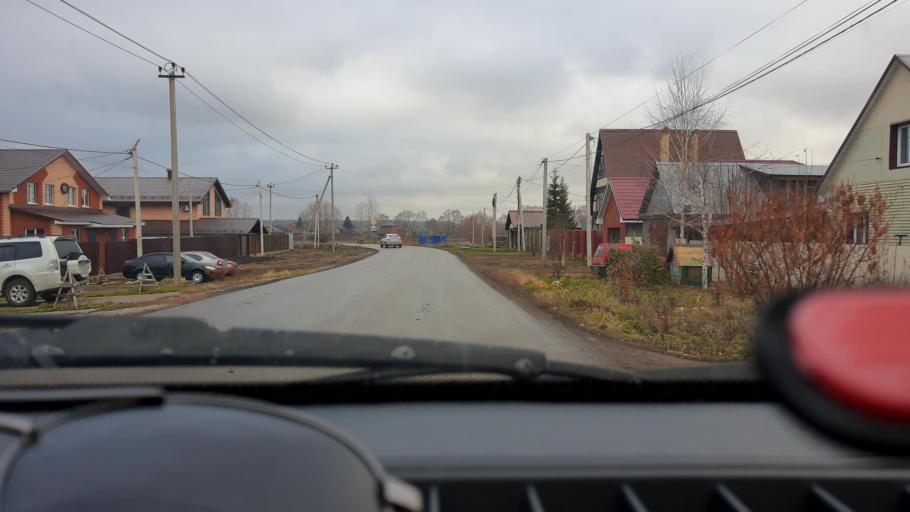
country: RU
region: Bashkortostan
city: Ufa
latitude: 54.6109
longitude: 55.9096
